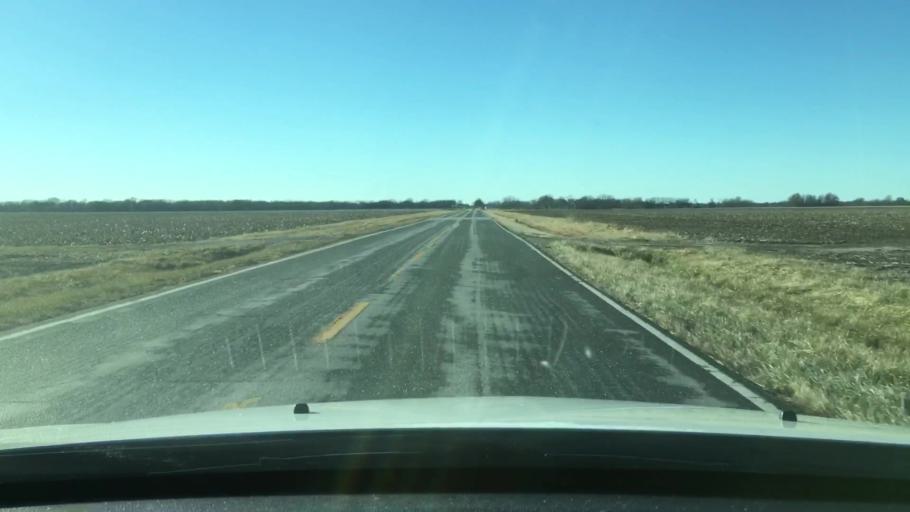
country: US
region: Missouri
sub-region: Audrain County
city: Vandalia
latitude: 39.2815
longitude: -91.6964
